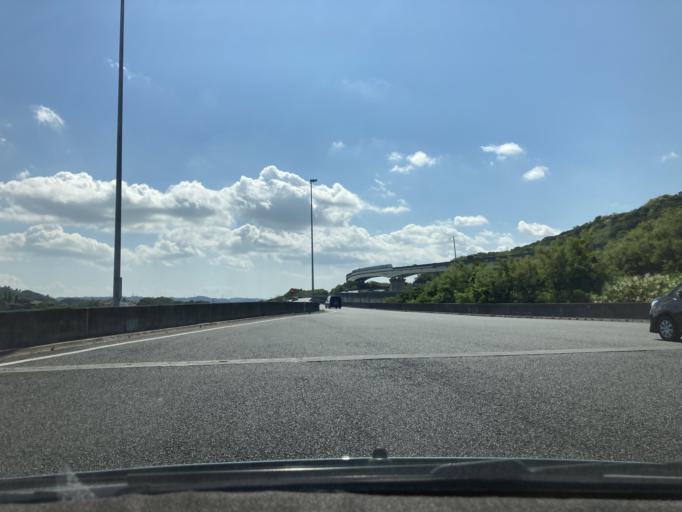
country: JP
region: Okinawa
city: Ginowan
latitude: 26.2212
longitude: 127.7391
